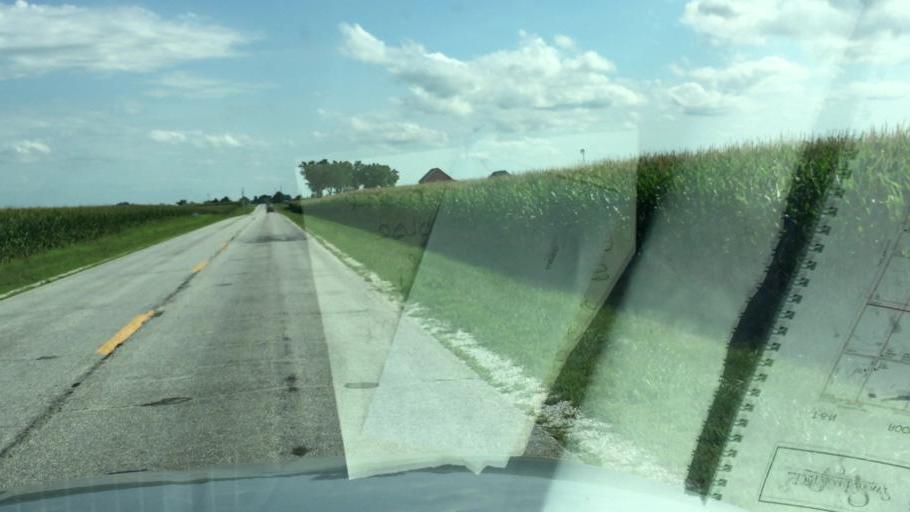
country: US
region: Illinois
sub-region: Hancock County
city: Nauvoo
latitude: 40.5105
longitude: -91.3084
